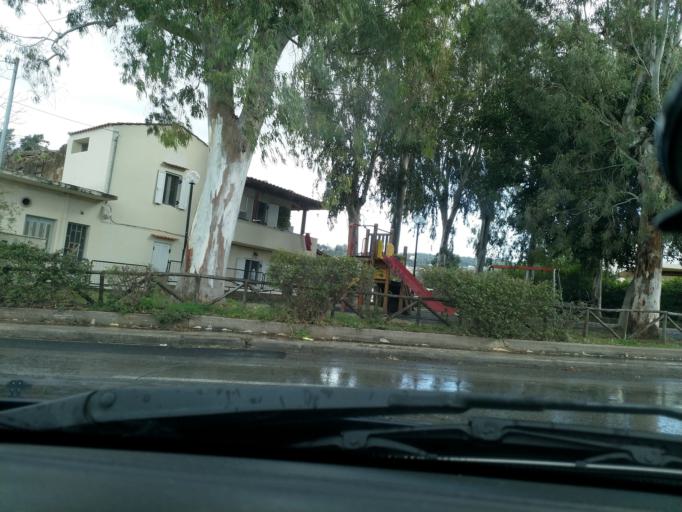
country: GR
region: Crete
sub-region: Nomos Chanias
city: Chania
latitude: 35.5112
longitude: 24.0424
